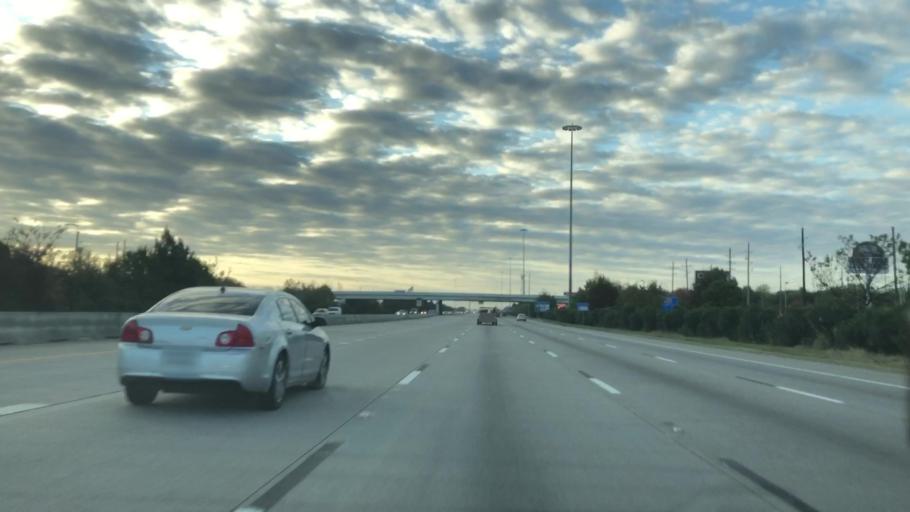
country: US
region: Texas
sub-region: Harris County
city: Spring
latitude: 30.0690
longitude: -95.4351
